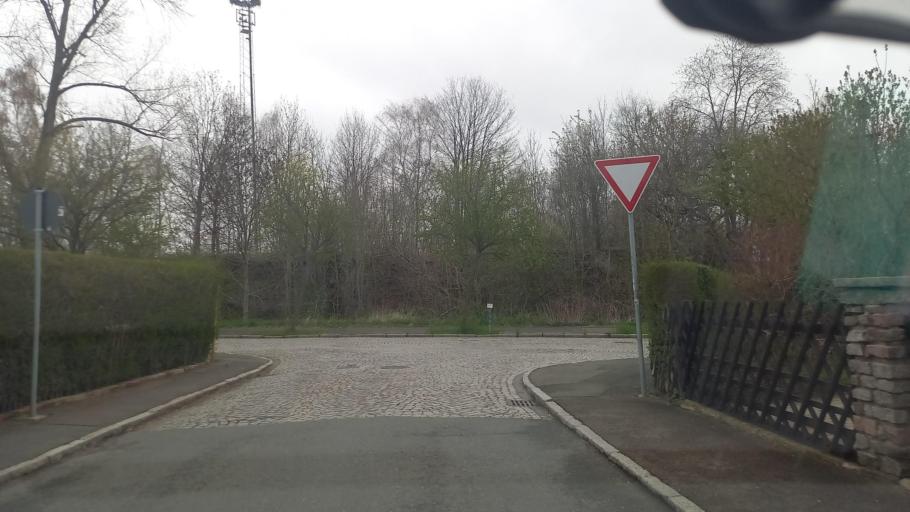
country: DE
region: Saxony
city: Zwickau
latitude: 50.7020
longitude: 12.4939
